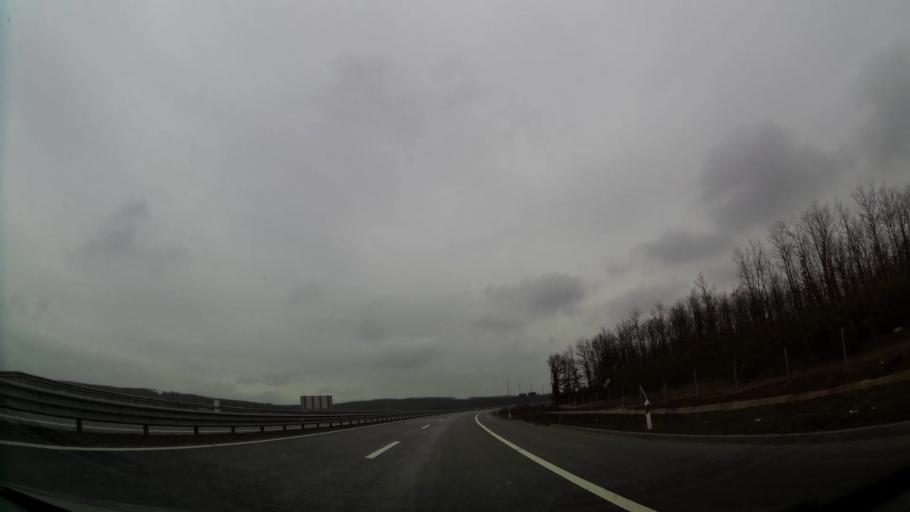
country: XK
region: Ferizaj
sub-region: Komuna e Ferizajt
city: Ferizaj
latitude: 42.3738
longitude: 21.2074
